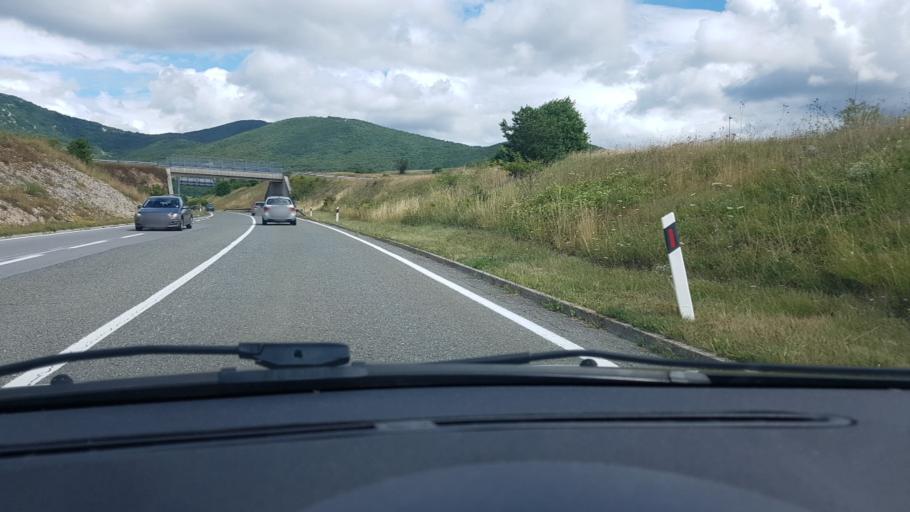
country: HR
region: Zadarska
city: Gracac
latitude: 44.5068
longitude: 15.7501
